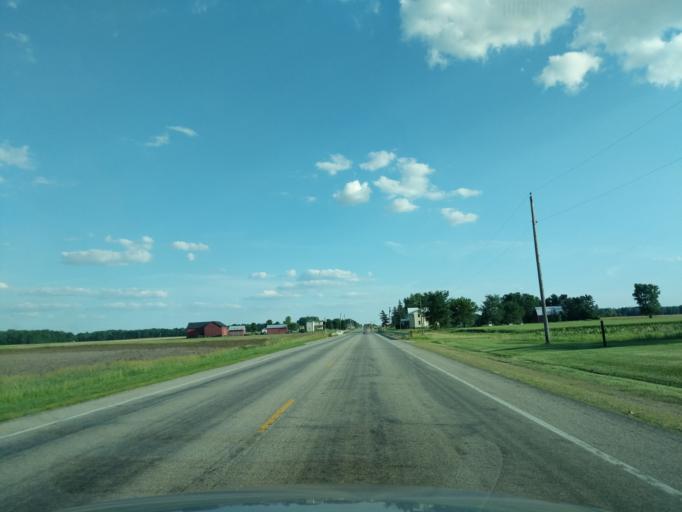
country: US
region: Indiana
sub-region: Whitley County
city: Columbia City
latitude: 41.0571
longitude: -85.4705
